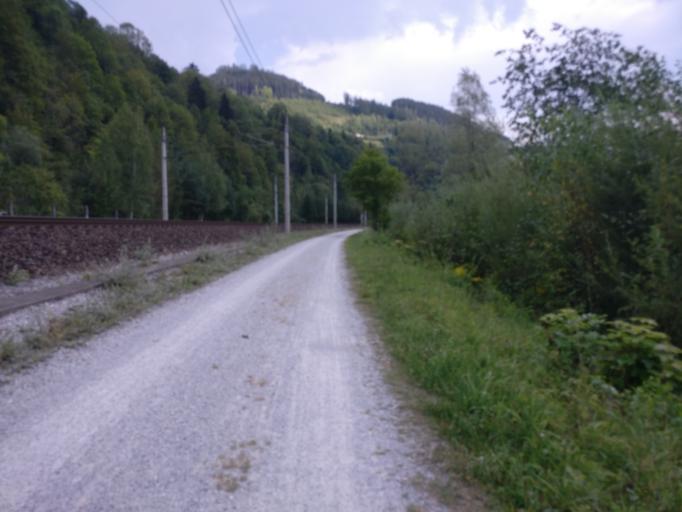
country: AT
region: Salzburg
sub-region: Politischer Bezirk Sankt Johann im Pongau
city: Pfarrwerfen
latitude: 47.4537
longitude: 13.2101
